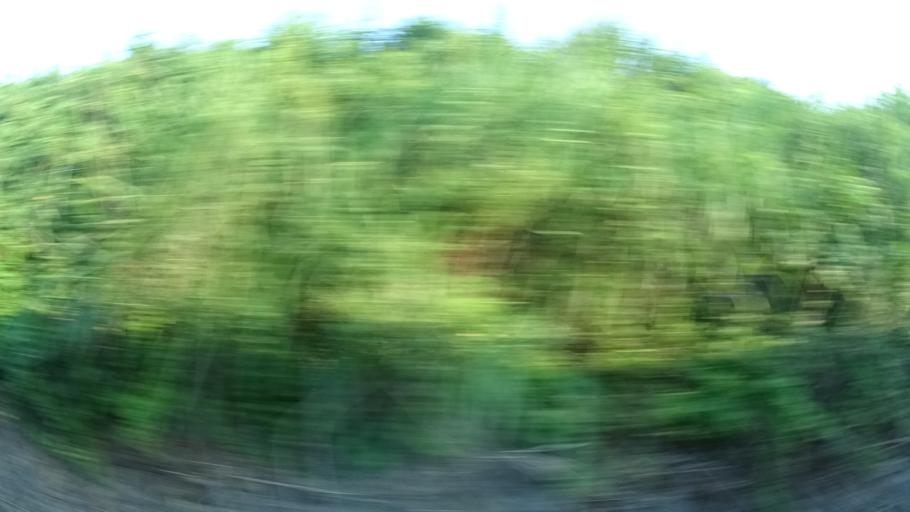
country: JP
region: Ibaraki
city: Mito-shi
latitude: 36.3840
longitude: 140.4305
